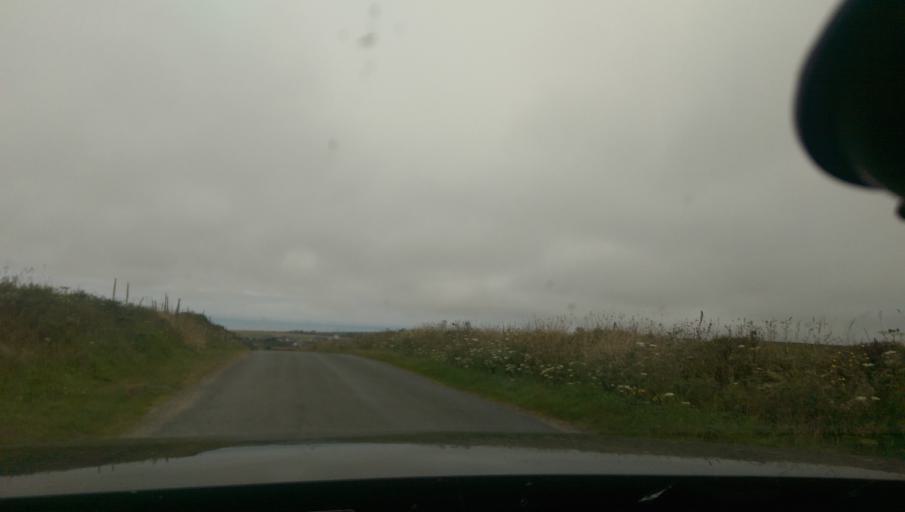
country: GB
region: England
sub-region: Cornwall
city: St. Buryan
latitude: 50.0977
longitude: -5.6525
